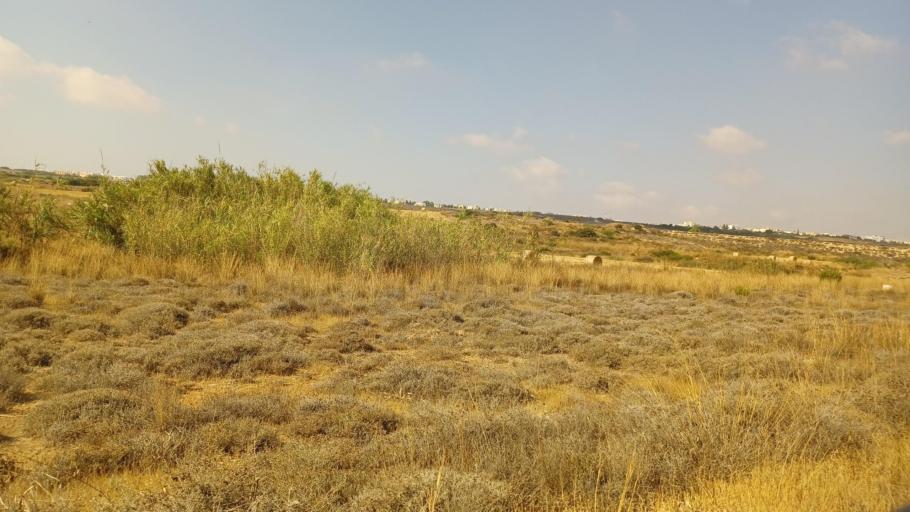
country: CY
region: Ammochostos
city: Deryneia
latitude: 35.0684
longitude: 33.9875
